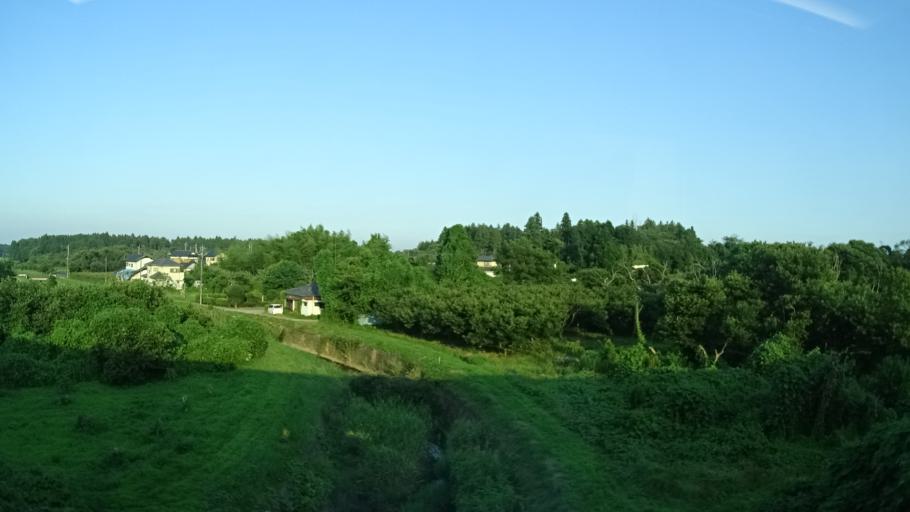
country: JP
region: Ibaraki
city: Tomobe
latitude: 36.3042
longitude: 140.2831
